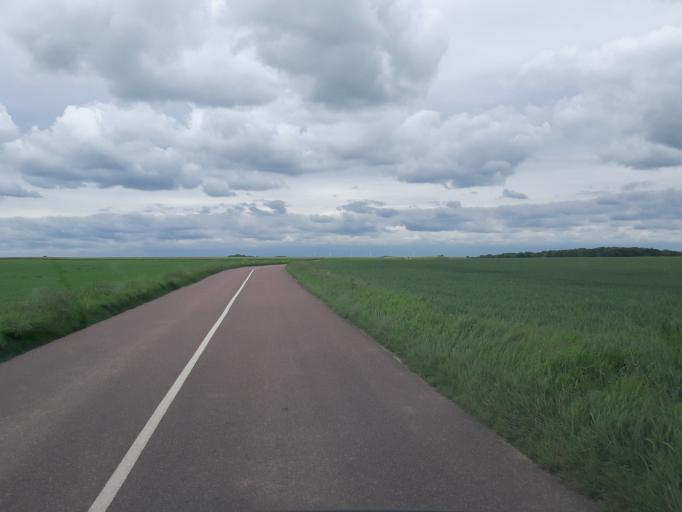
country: FR
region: Ile-de-France
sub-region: Departement de l'Essonne
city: Saclas
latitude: 48.3408
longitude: 2.1291
